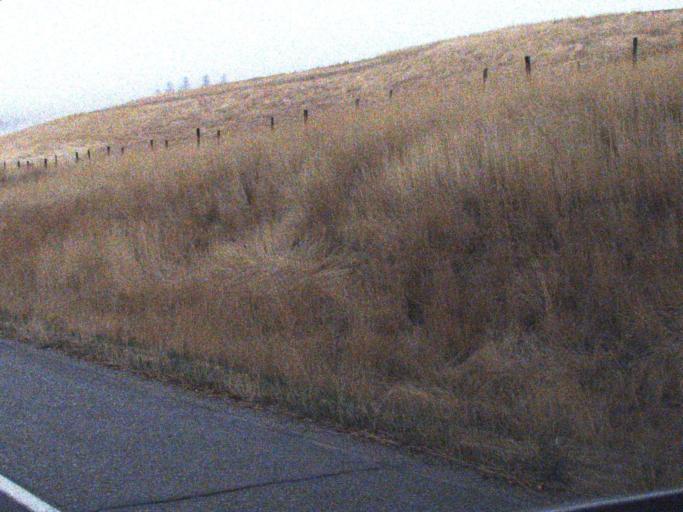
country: US
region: Washington
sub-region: Stevens County
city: Kettle Falls
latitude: 48.6054
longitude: -118.0266
